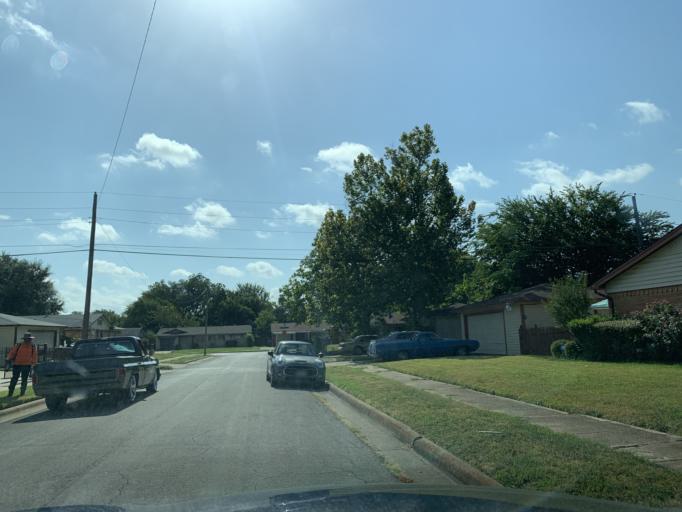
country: US
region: Texas
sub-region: Dallas County
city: Hutchins
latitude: 32.6902
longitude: -96.7873
